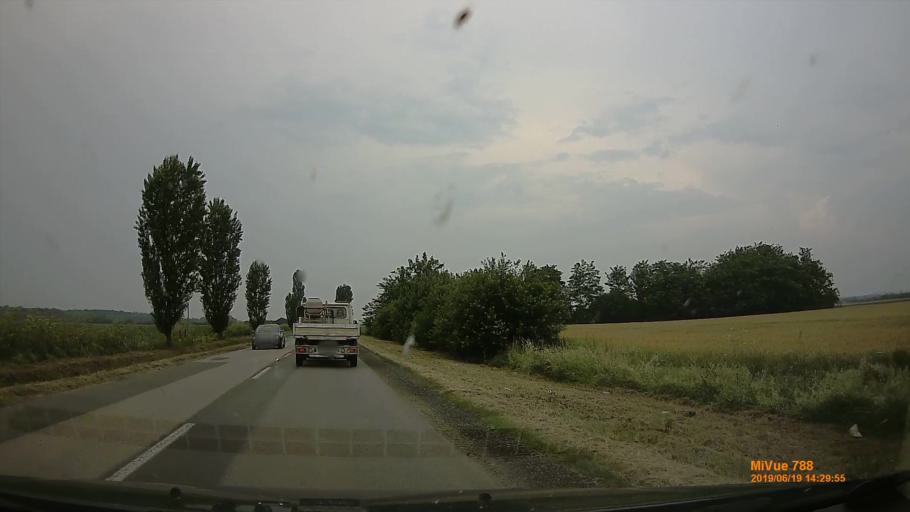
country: HU
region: Baranya
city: Szigetvar
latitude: 46.0574
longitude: 17.7784
